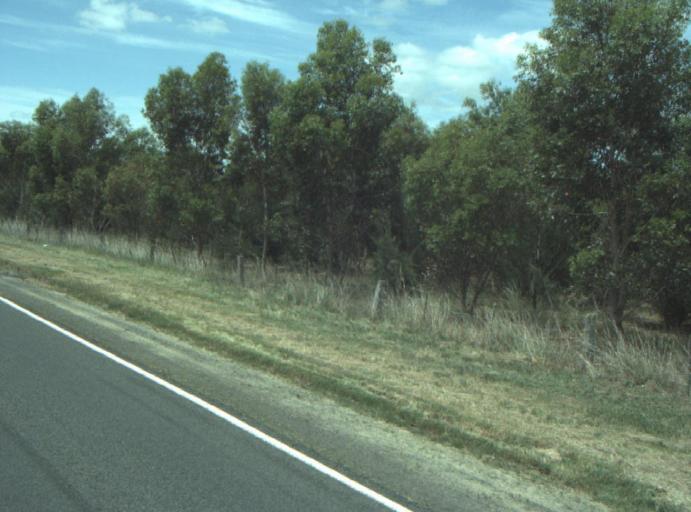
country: AU
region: Victoria
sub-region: Greater Geelong
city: Bell Post Hill
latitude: -38.0067
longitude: 144.2848
